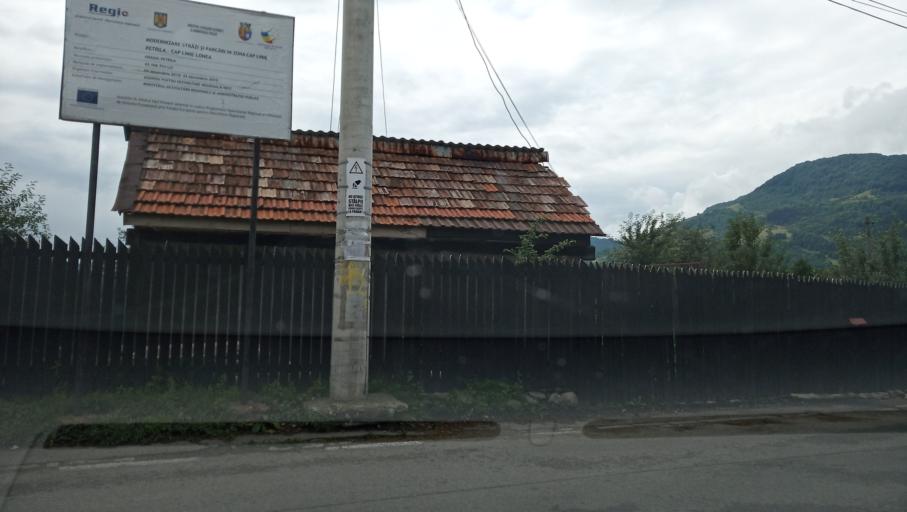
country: RO
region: Hunedoara
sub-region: Oras Petrila
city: Petrila
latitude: 45.4449
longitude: 23.4094
